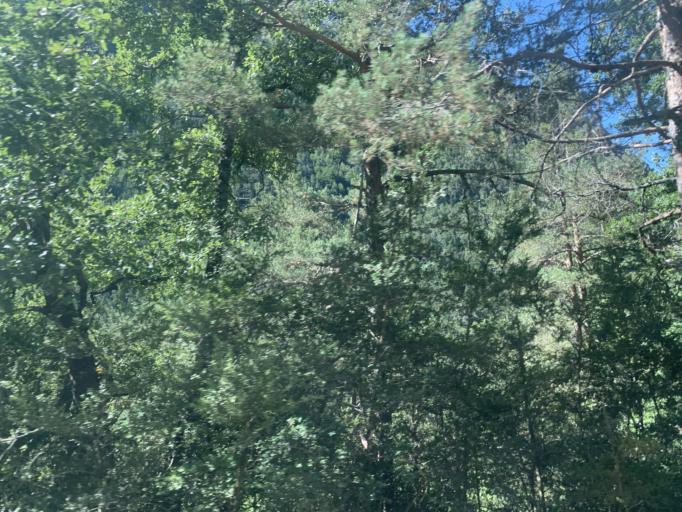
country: ES
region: Aragon
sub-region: Provincia de Huesca
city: Broto
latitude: 42.6546
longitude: -0.0892
